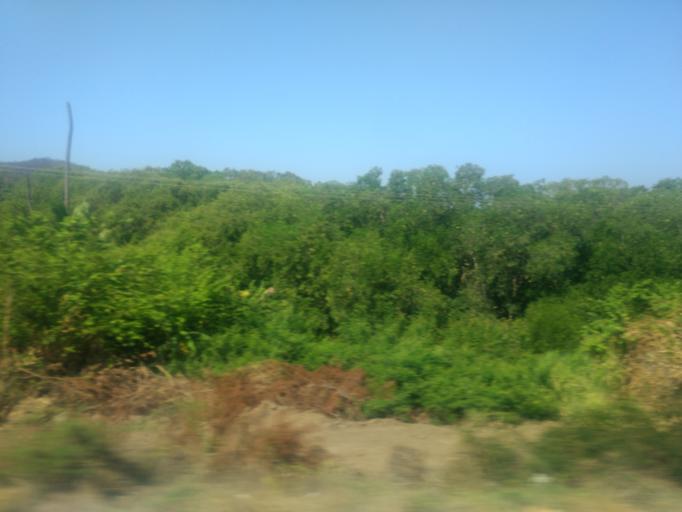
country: MX
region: Colima
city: El Colomo
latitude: 19.0302
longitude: -104.2446
